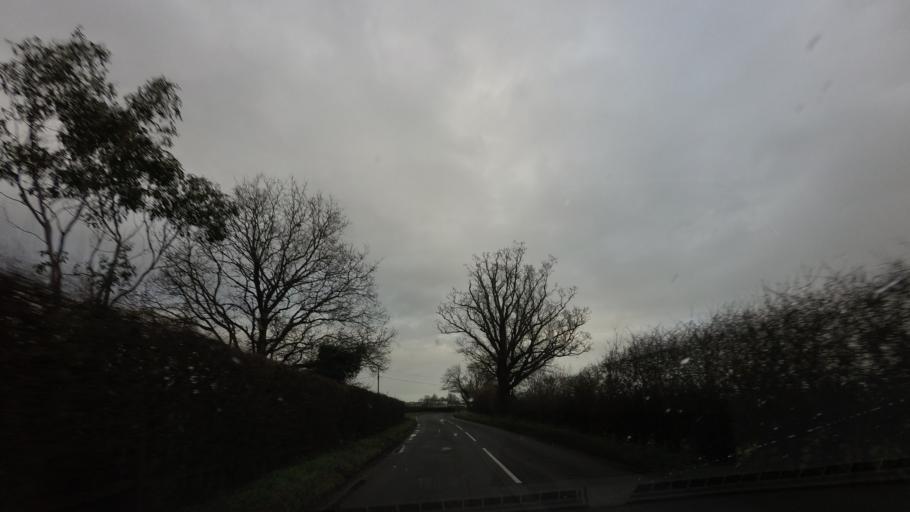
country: GB
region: England
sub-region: Kent
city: Marden
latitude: 51.1906
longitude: 0.5060
